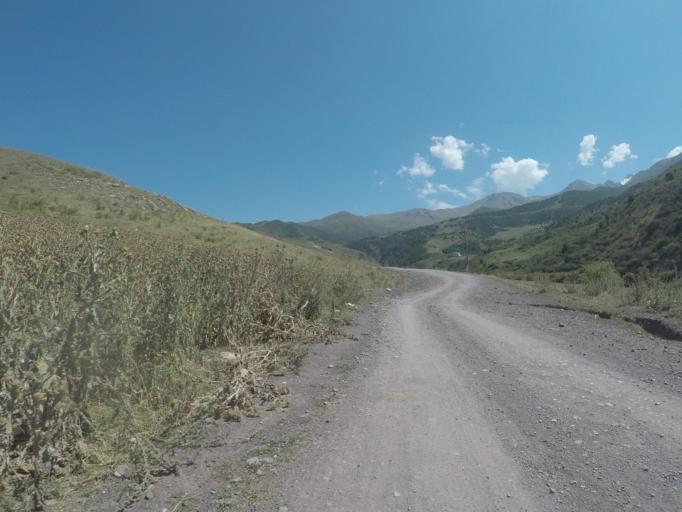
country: KG
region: Chuy
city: Bishkek
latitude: 42.6502
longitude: 74.5086
